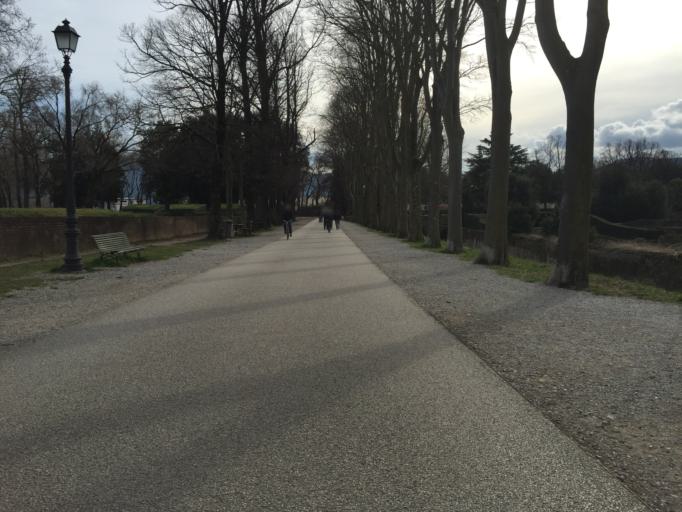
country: IT
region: Tuscany
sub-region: Provincia di Lucca
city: Lucca
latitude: 43.8428
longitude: 10.5140
